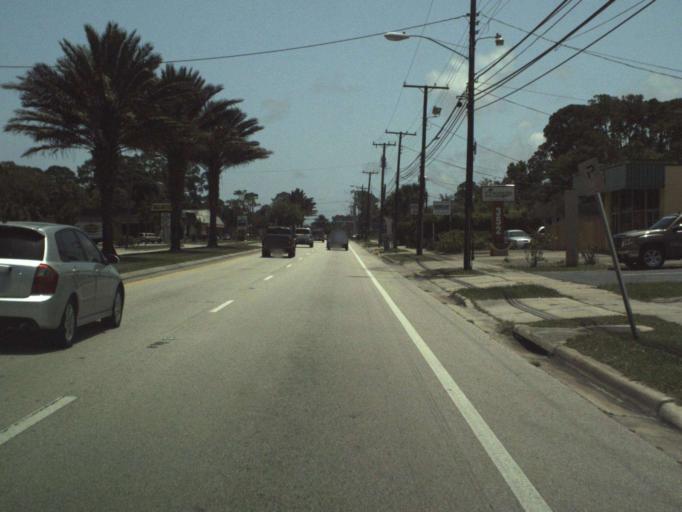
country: US
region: Florida
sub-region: Volusia County
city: Ormond Beach
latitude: 29.2745
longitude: -81.0578
